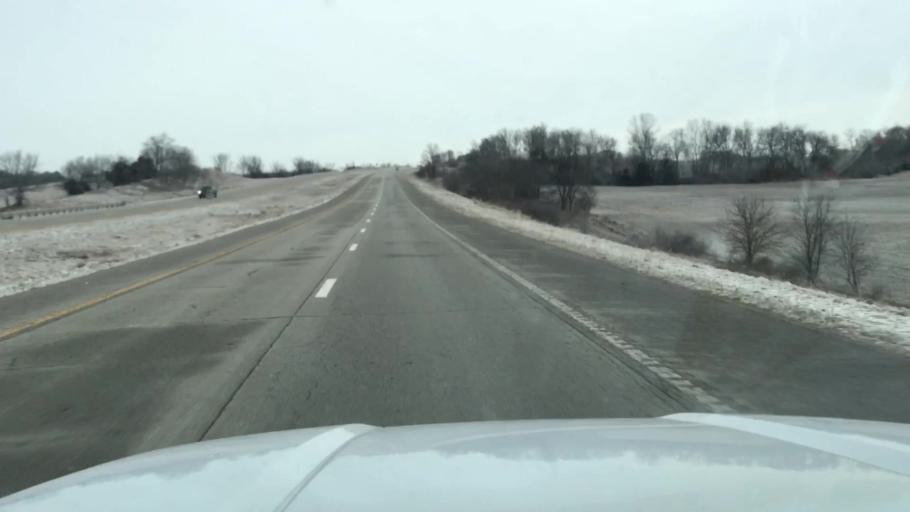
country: US
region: Missouri
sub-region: Andrew County
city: Savannah
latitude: 39.9074
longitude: -94.8588
